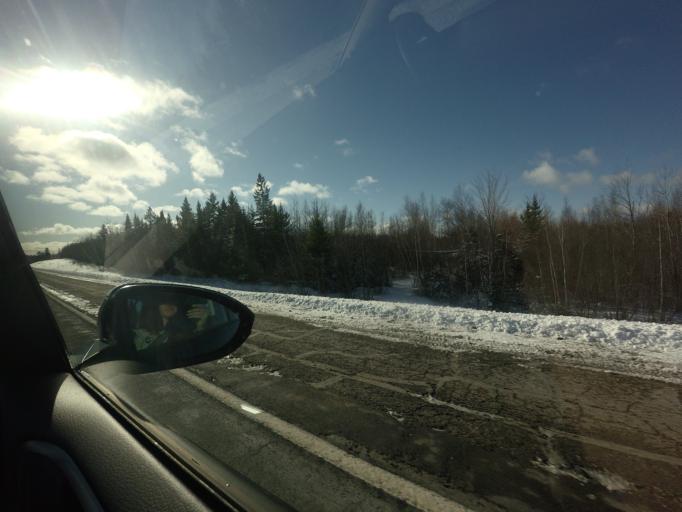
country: CA
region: New Brunswick
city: Fredericton
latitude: 45.8951
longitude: -66.6483
